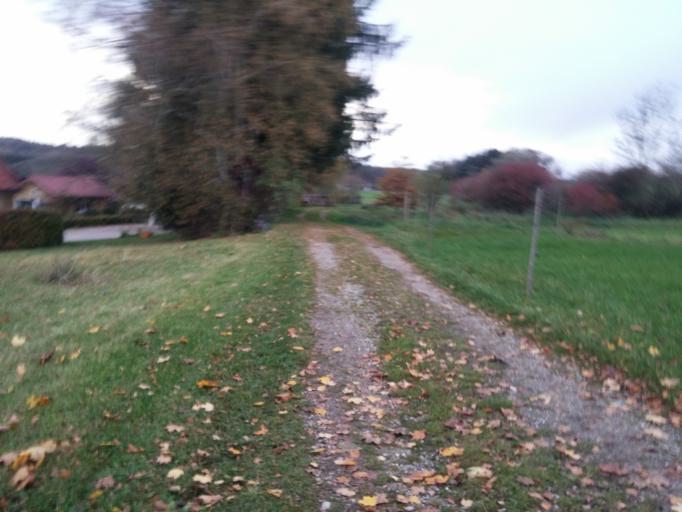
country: DE
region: Bavaria
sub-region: Upper Bavaria
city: Grafing bei Munchen
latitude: 48.0220
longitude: 11.9878
